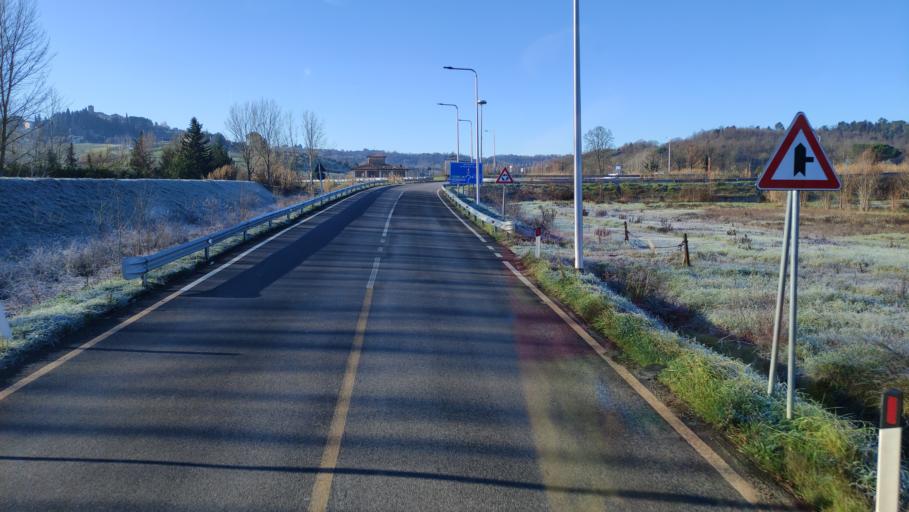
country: IT
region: Tuscany
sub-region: Province of Florence
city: Castelfiorentino
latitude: 43.6448
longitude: 10.9403
